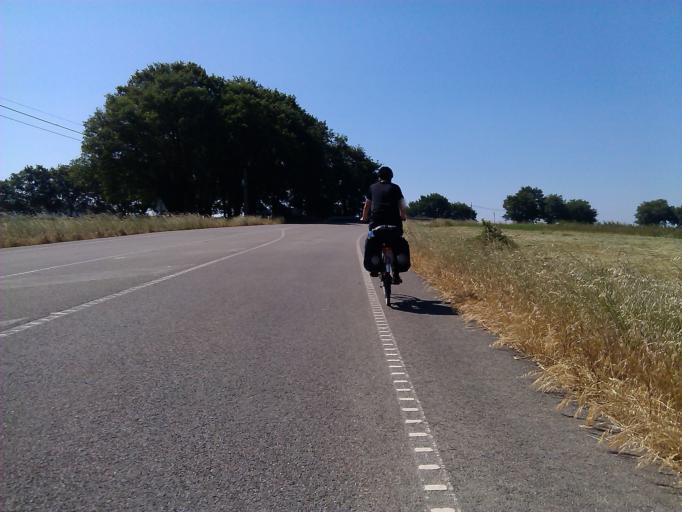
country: ES
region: Galicia
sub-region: Provincia de Lugo
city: Samos
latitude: 42.7401
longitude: -7.3695
